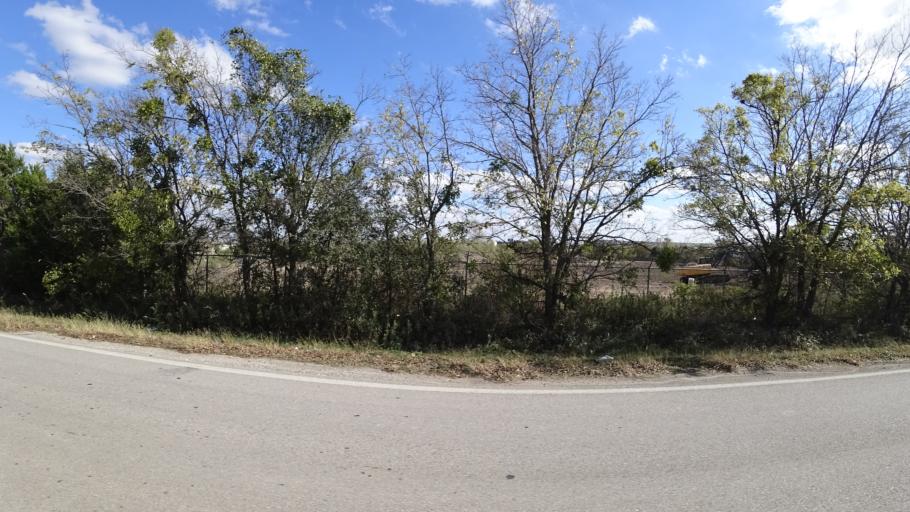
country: US
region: Texas
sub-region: Travis County
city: Wells Branch
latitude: 30.4678
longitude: -97.6761
